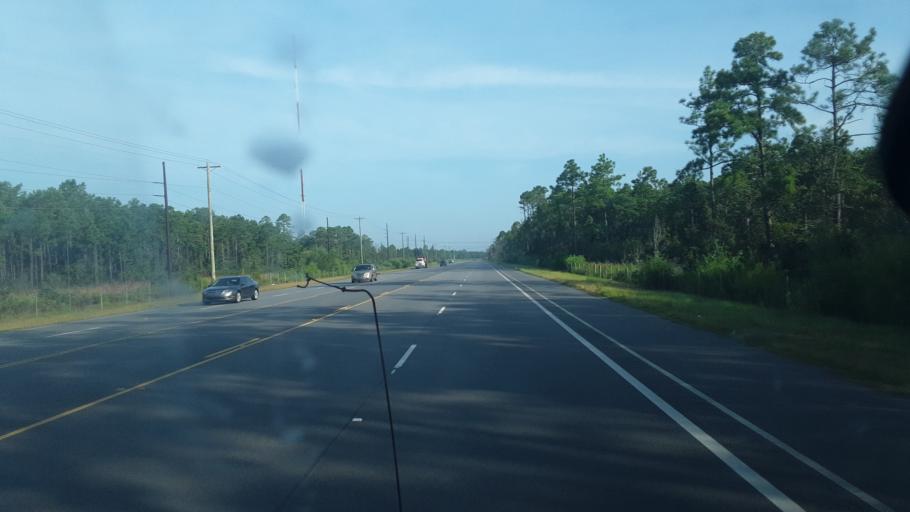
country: US
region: South Carolina
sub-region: Horry County
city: Myrtle Beach
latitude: 33.7804
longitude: -78.8743
